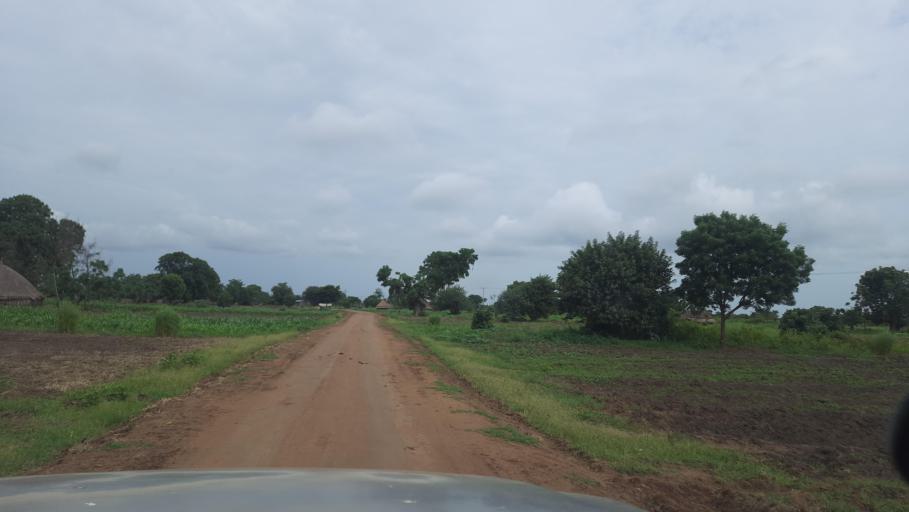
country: ET
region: Gambela
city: Gambela
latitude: 8.3273
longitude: 33.7145
